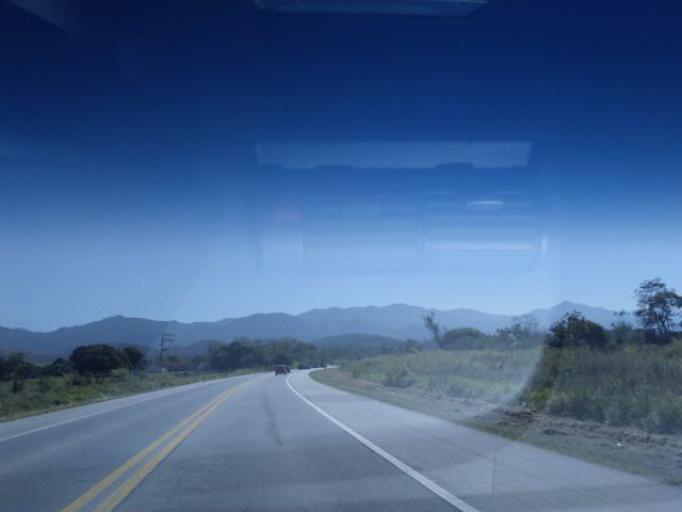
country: BR
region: Sao Paulo
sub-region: Taubate
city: Taubate
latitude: -22.9893
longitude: -45.6478
